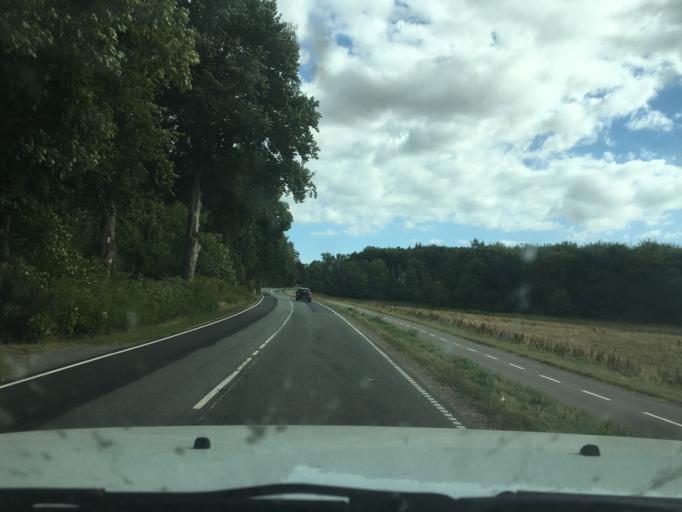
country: DK
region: Central Jutland
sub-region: Syddjurs Kommune
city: Hornslet
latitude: 56.2998
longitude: 10.3165
